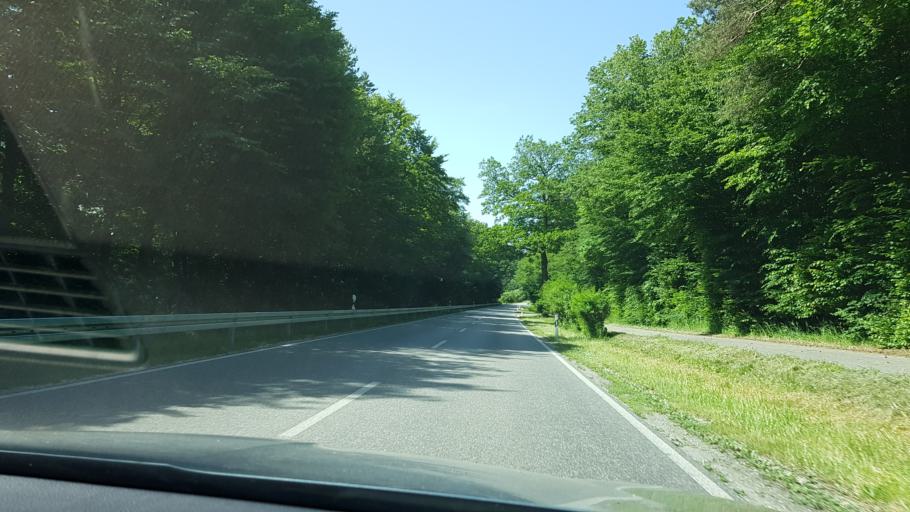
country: DE
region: Bavaria
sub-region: Upper Bavaria
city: Schongeising
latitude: 48.1335
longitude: 11.1921
